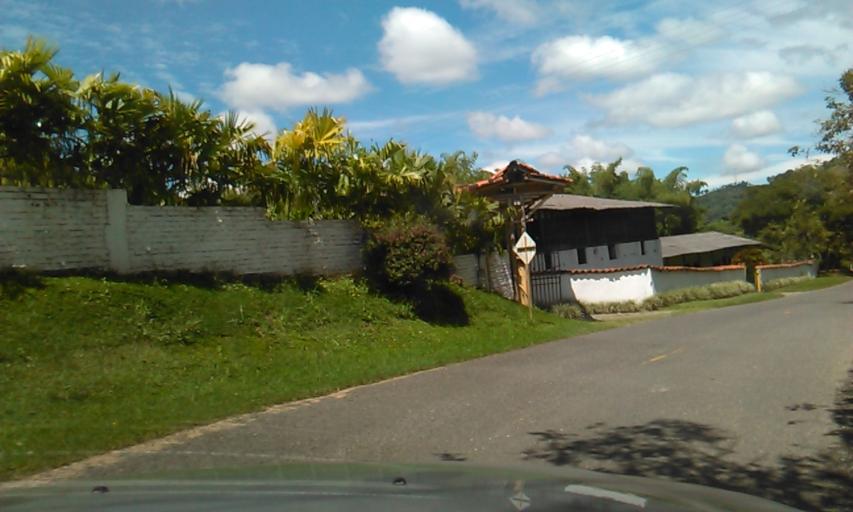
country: CO
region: Quindio
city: Cordoba
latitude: 4.4036
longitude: -75.6902
